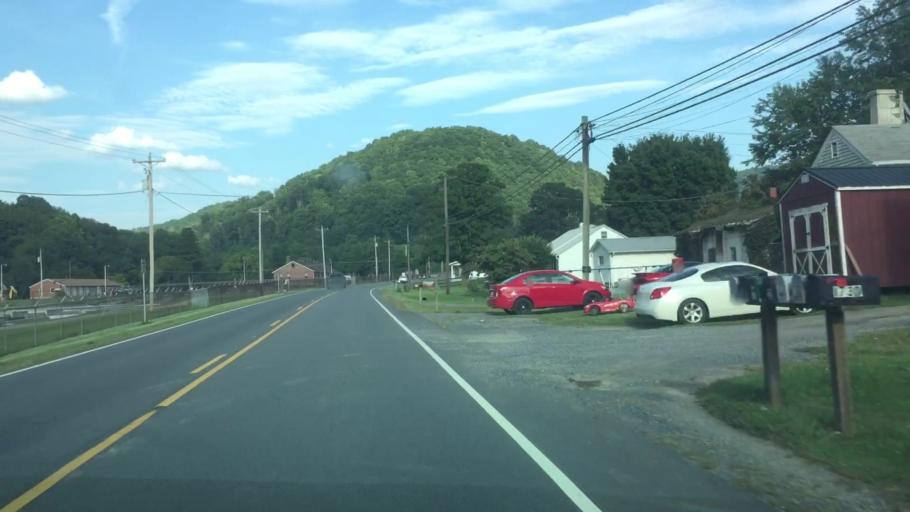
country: US
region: Virginia
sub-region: Smyth County
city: Marion
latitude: 36.8235
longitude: -81.4806
